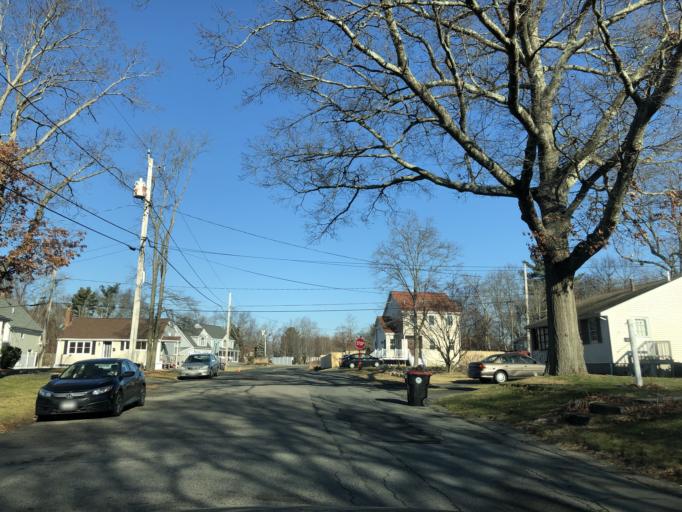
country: US
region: Massachusetts
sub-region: Plymouth County
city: Brockton
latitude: 42.1009
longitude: -71.0053
